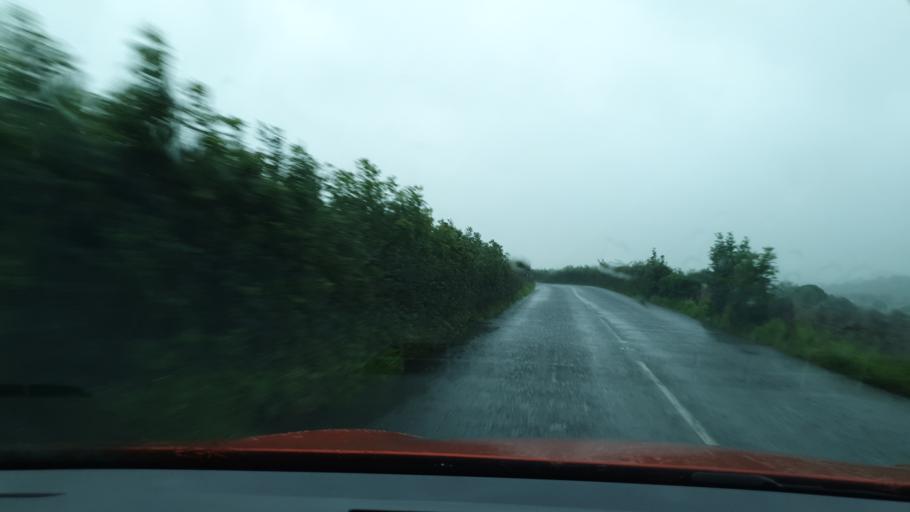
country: GB
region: England
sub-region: Cumbria
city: Millom
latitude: 54.2757
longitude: -3.2212
